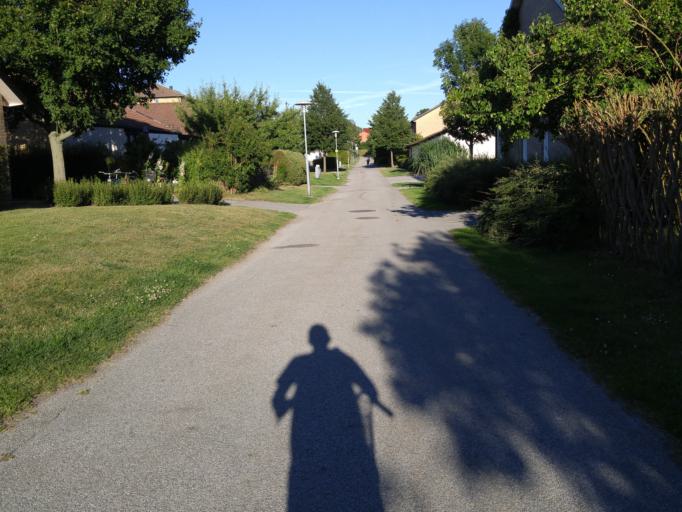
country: SE
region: Skane
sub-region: Lunds Kommun
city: Lund
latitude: 55.7293
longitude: 13.2105
